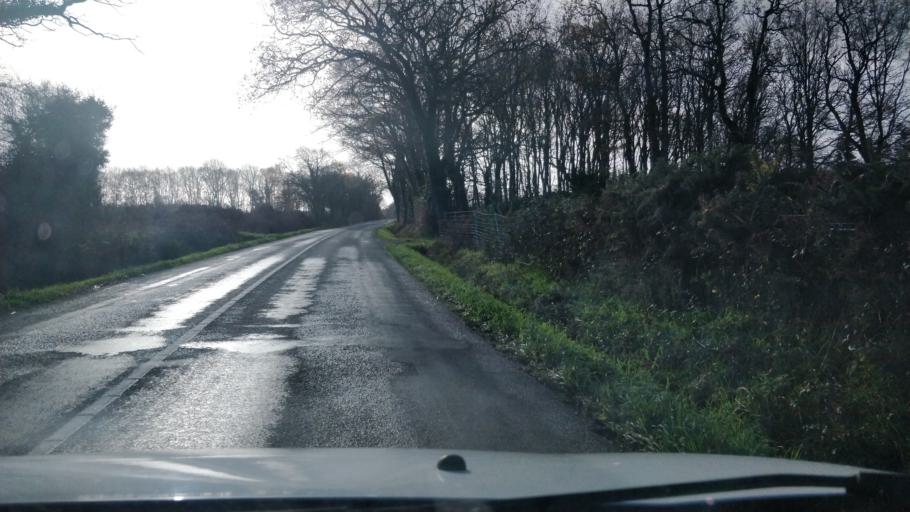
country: FR
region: Pays de la Loire
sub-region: Departement de la Loire-Atlantique
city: Saint-Molf
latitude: 47.3678
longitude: -2.4315
